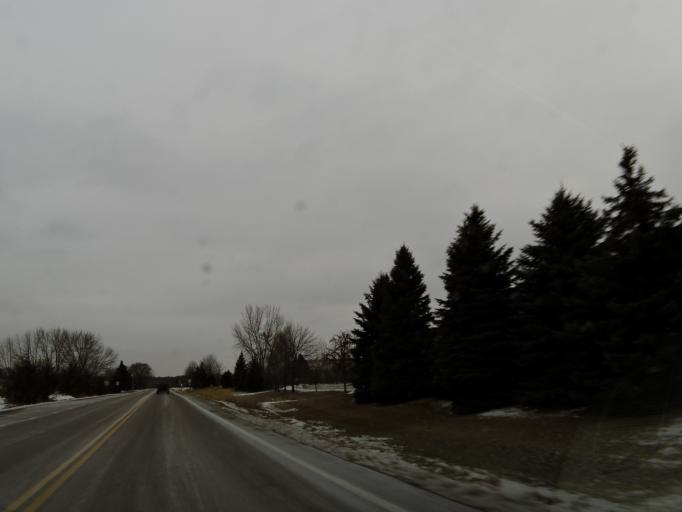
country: US
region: Minnesota
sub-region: Scott County
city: Jordan
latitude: 44.6829
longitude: -93.6398
